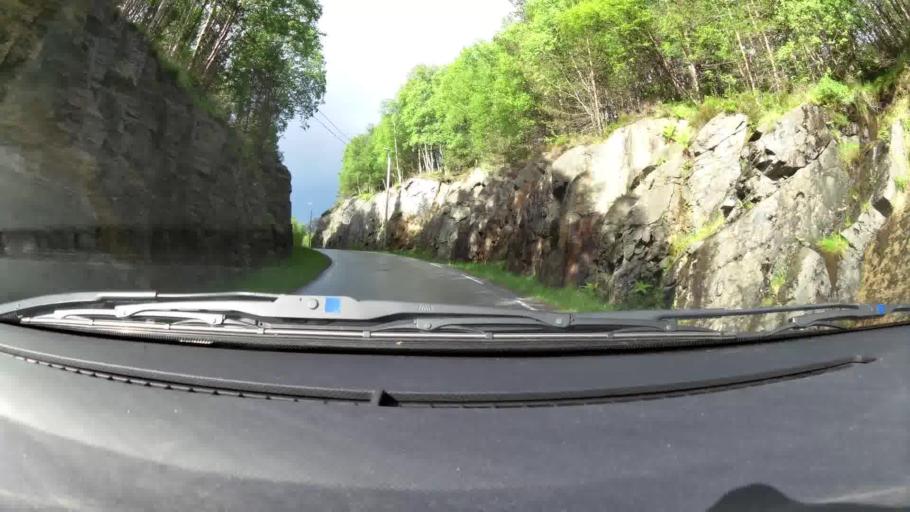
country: NO
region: More og Romsdal
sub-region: Kristiansund
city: Kristiansund
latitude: 63.0535
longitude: 7.7092
